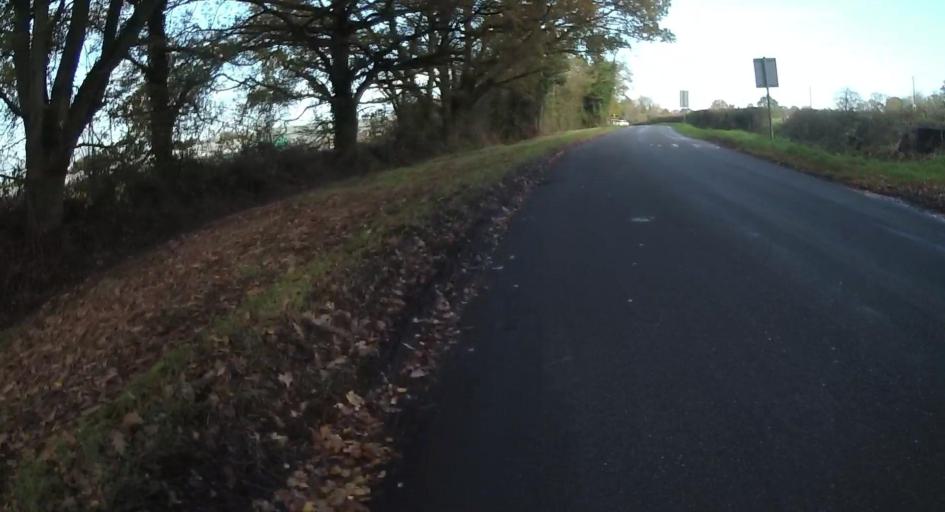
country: GB
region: England
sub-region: West Berkshire
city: Arborfield
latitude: 51.3936
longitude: -0.9145
